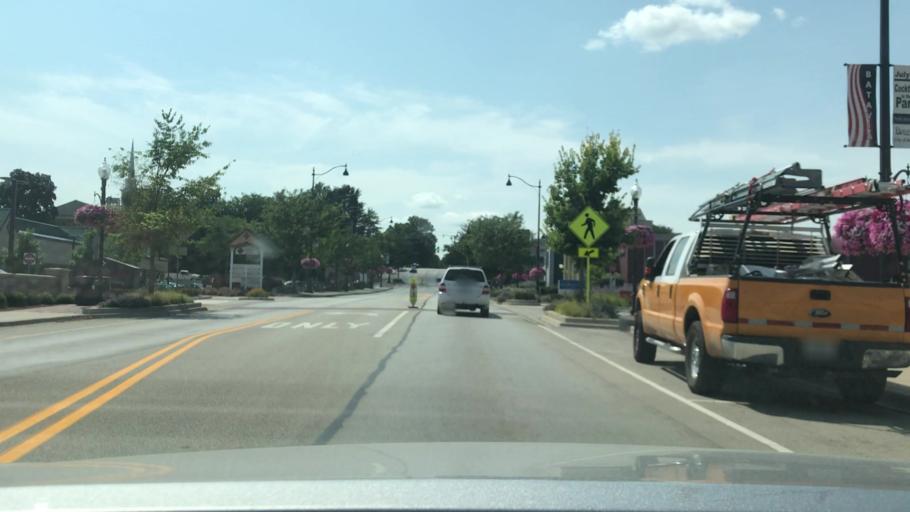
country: US
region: Illinois
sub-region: Kane County
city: Batavia
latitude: 41.8500
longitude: -88.3086
